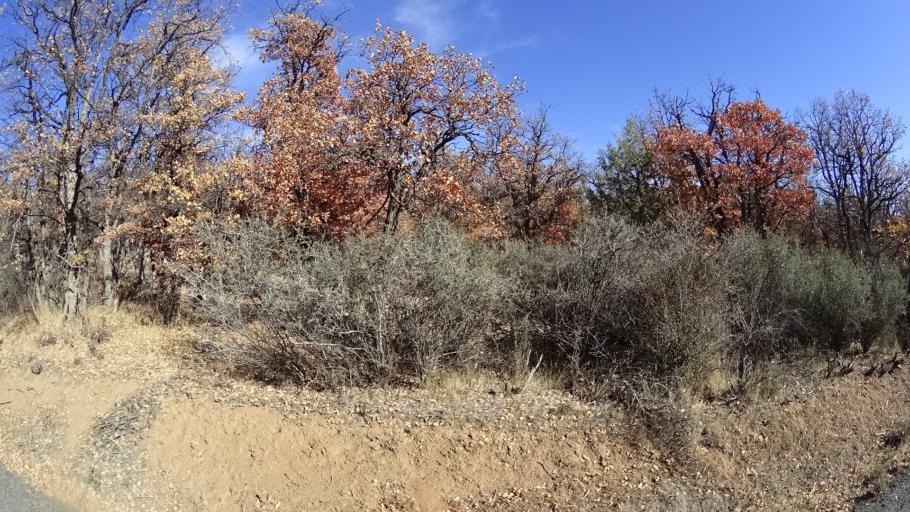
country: US
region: California
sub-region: Siskiyou County
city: Yreka
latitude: 41.7726
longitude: -122.6423
